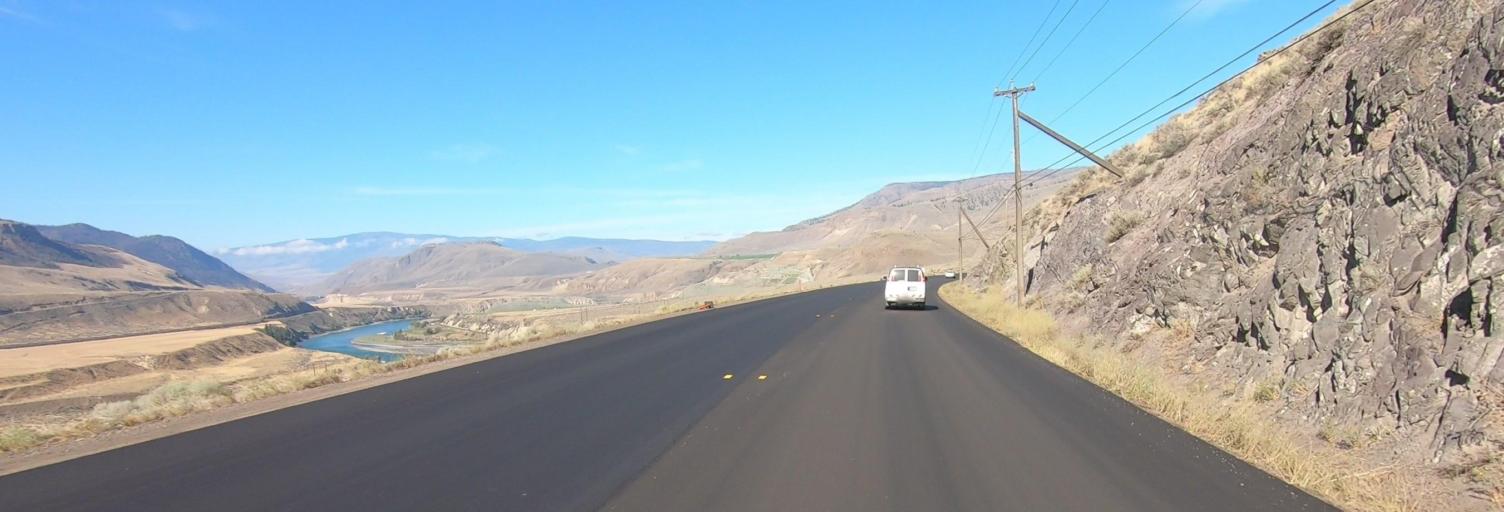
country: CA
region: British Columbia
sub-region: Thompson-Nicola Regional District
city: Ashcroft
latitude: 50.7910
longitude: -121.0823
